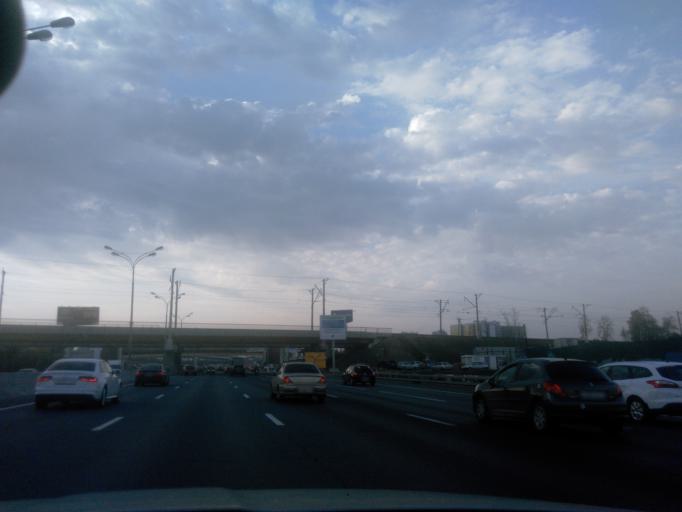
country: RU
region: Moskovskaya
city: Marfino
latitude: 55.7199
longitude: 37.3826
